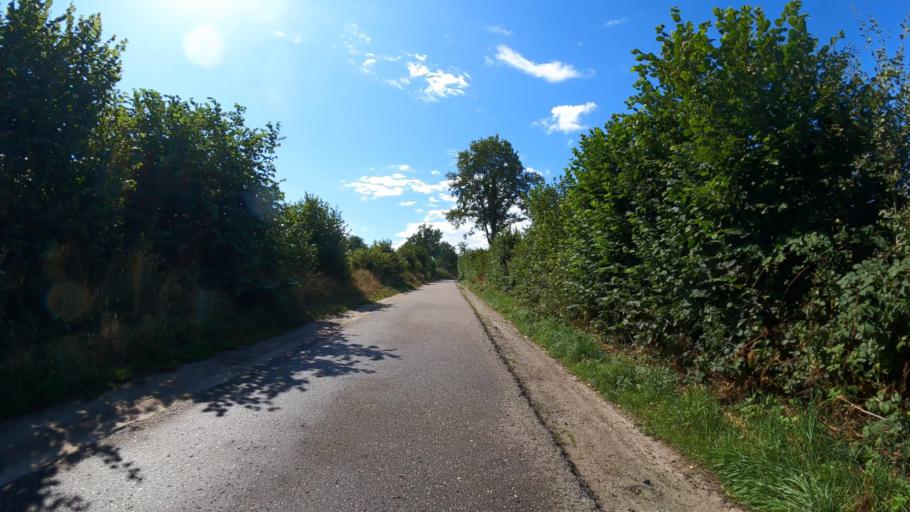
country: DE
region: Schleswig-Holstein
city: Armstedt
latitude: 53.9650
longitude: 9.8579
